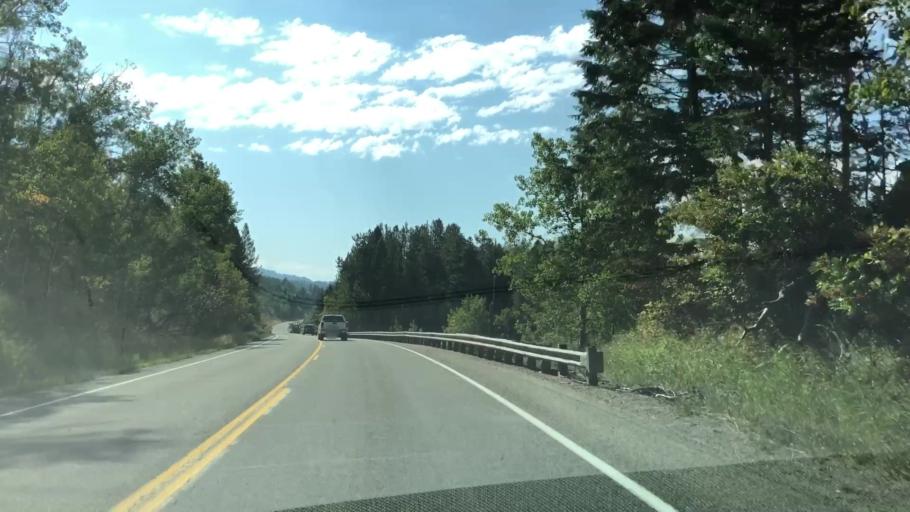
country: US
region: Idaho
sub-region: Teton County
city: Victor
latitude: 43.2973
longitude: -111.1288
